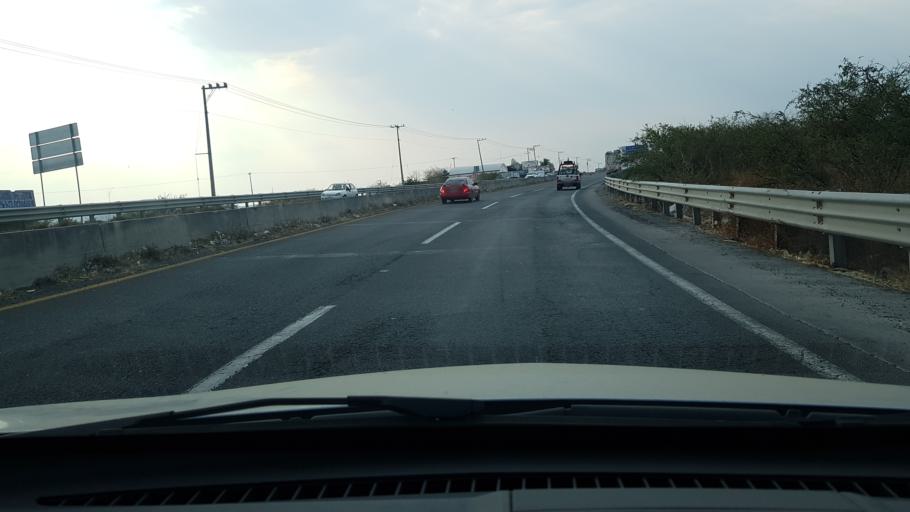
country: MX
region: Morelos
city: Amayuca
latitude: 18.7216
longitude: -98.8038
